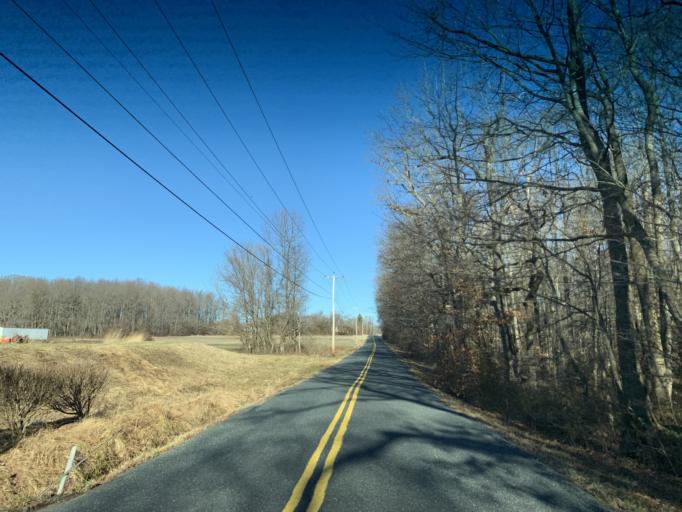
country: US
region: Maryland
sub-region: Harford County
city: Riverside
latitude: 39.5374
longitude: -76.2384
